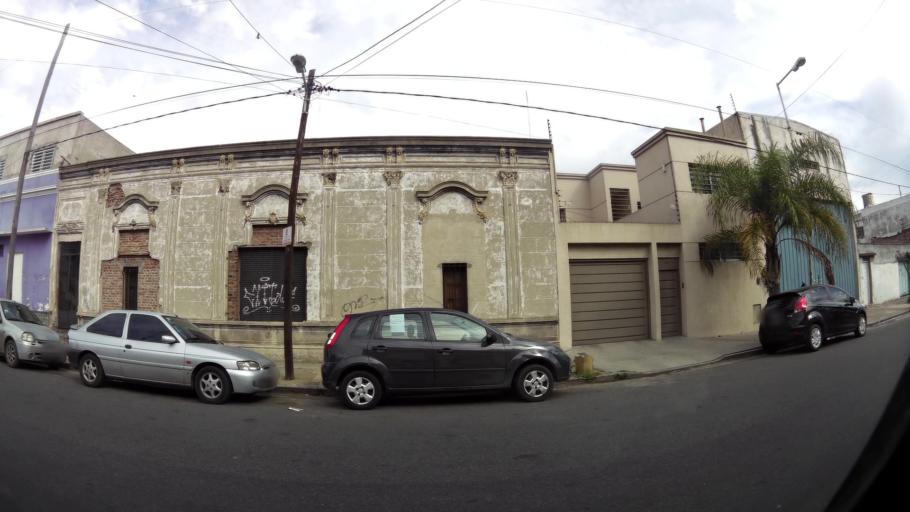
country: AR
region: Buenos Aires
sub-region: Partido de Avellaneda
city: Avellaneda
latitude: -34.6766
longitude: -58.3839
